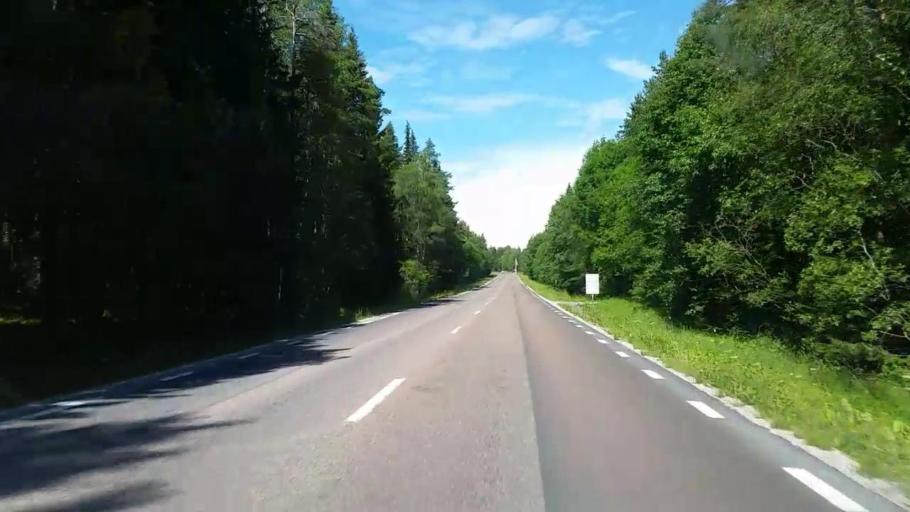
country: SE
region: Dalarna
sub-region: Rattviks Kommun
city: Raettvik
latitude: 61.0314
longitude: 15.2058
